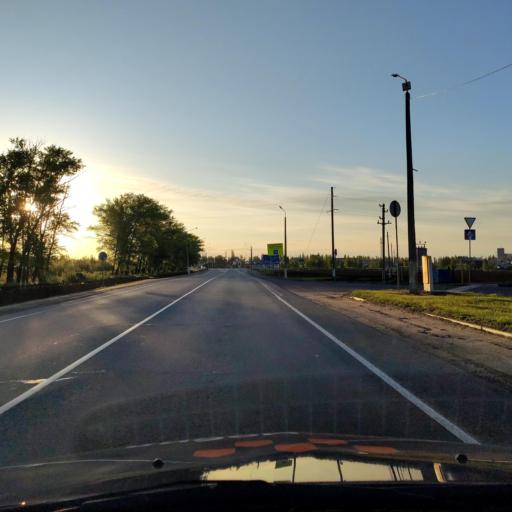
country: RU
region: Orjol
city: Livny
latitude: 52.4410
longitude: 37.5704
